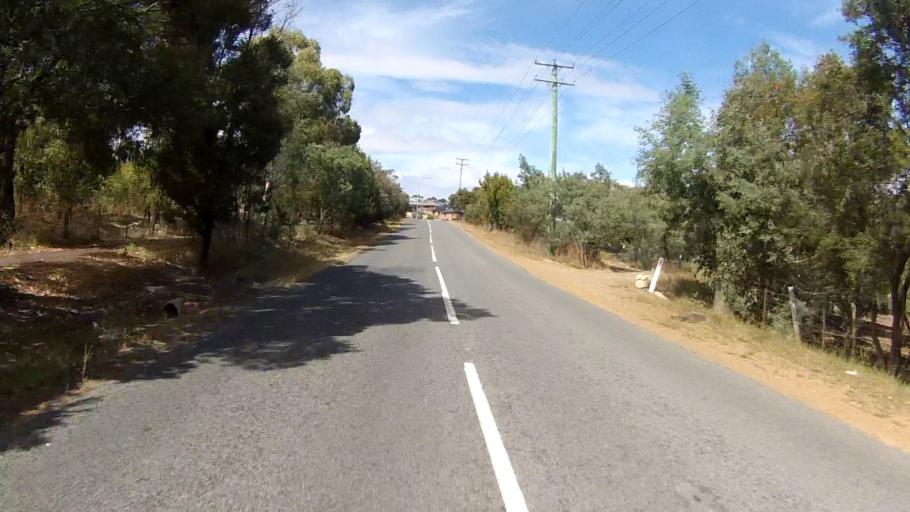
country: AU
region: Tasmania
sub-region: Clarence
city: Lindisfarne
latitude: -42.8192
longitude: 147.3512
